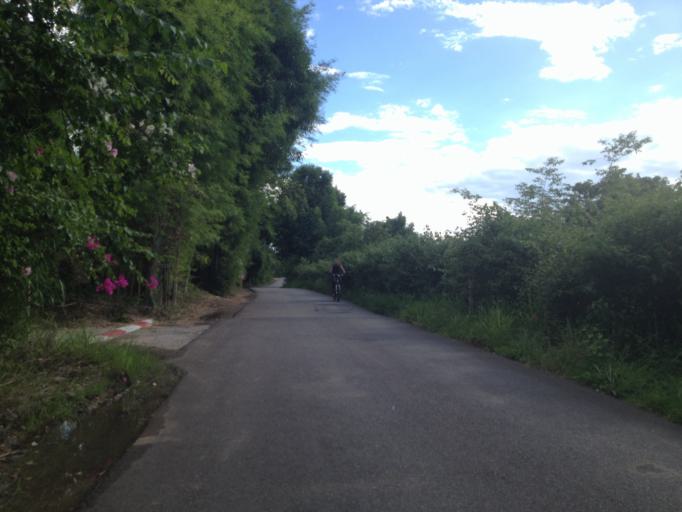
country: TH
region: Chiang Mai
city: Hang Dong
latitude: 18.7011
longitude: 98.8970
